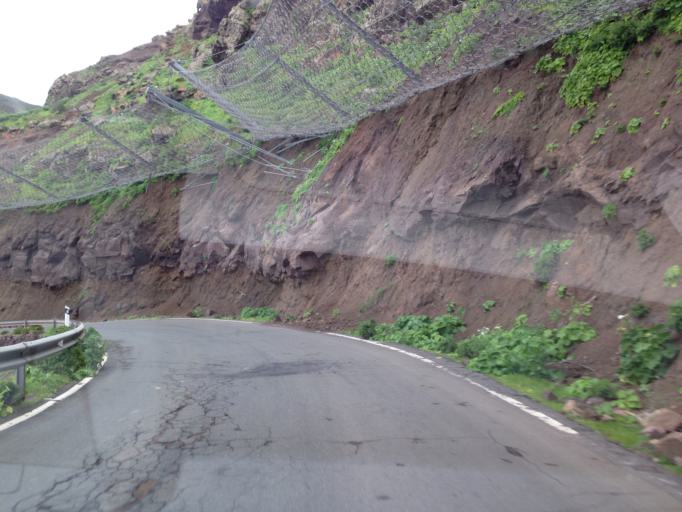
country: ES
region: Canary Islands
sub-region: Provincia de Las Palmas
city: San Nicolas
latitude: 28.0289
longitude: -15.7676
